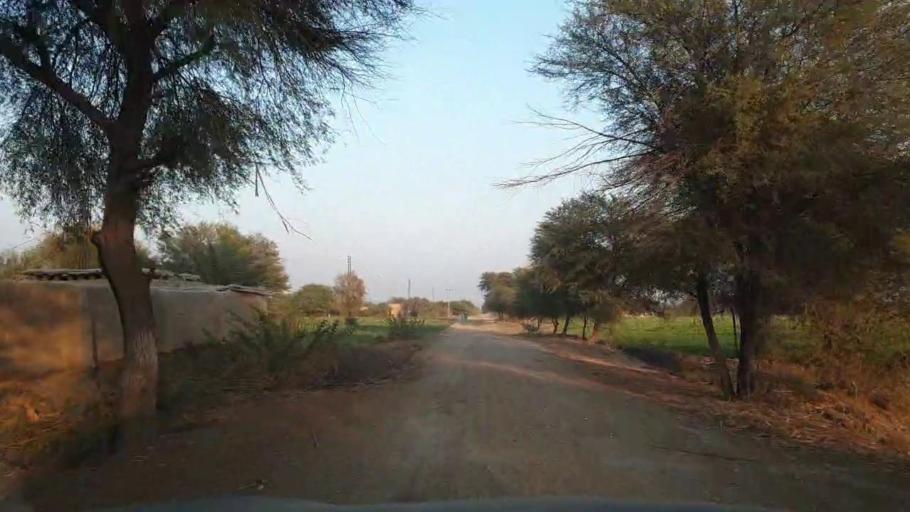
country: PK
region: Sindh
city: Mirpur Khas
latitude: 25.5758
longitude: 68.8560
